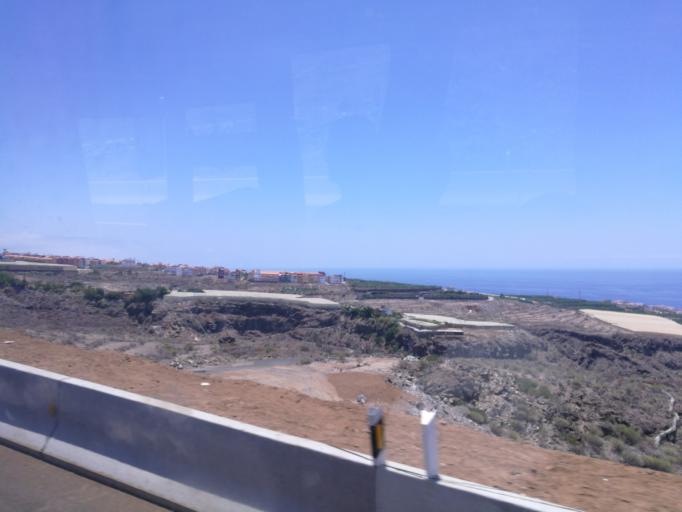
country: ES
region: Canary Islands
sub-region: Provincia de Santa Cruz de Tenerife
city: Guia de Isora
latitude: 28.1882
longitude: -16.7948
